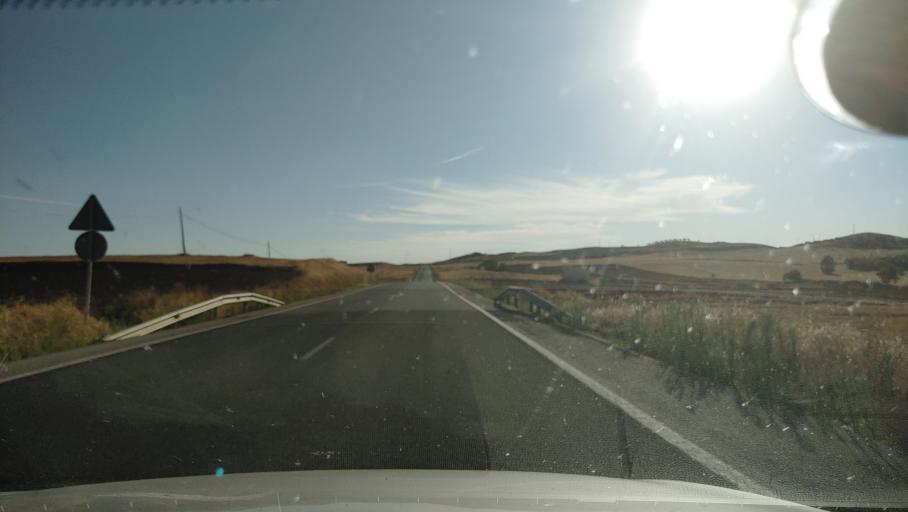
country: ES
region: Castille-La Mancha
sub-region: Provincia de Ciudad Real
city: Fuenllana
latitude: 38.7511
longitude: -2.9648
